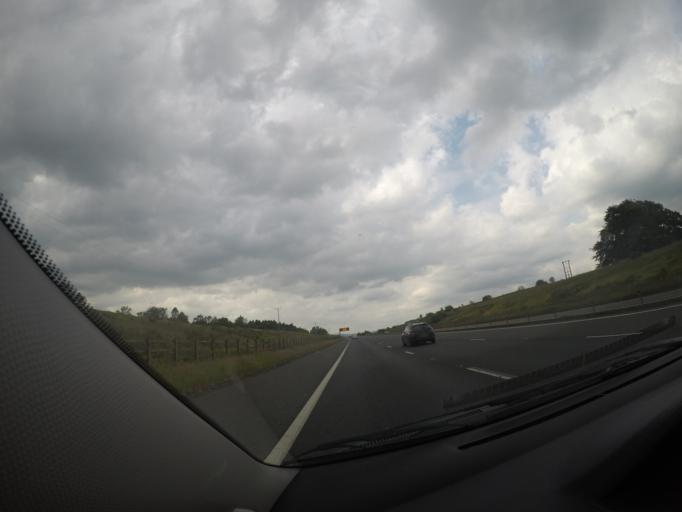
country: GB
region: Scotland
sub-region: Dumfries and Galloway
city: Moffat
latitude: 55.2805
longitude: -3.4272
